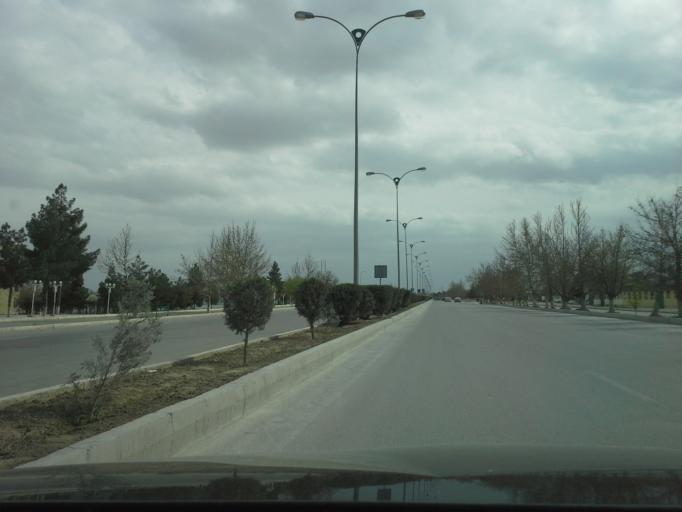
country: TM
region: Ahal
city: Abadan
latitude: 38.0420
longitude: 58.1860
